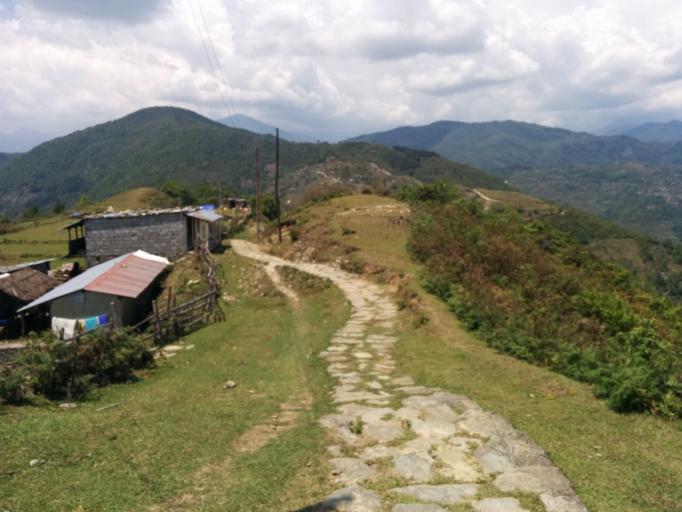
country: NP
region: Western Region
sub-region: Gandaki Zone
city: Pokhara
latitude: 28.2591
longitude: 83.8211
